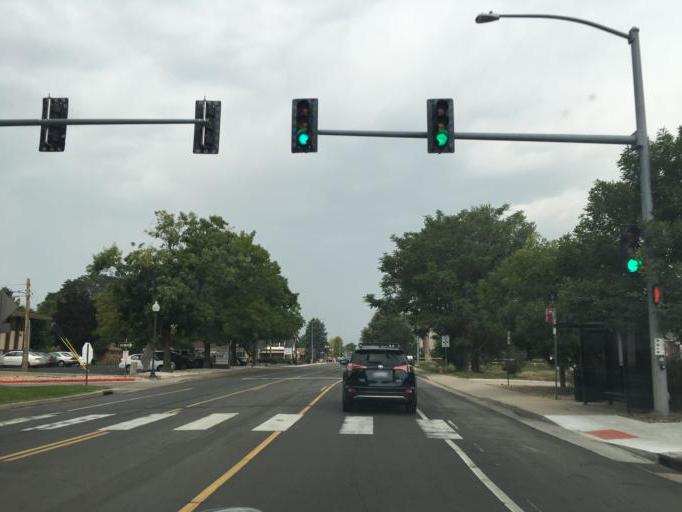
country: US
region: Colorado
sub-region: Jefferson County
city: Wheat Ridge
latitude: 39.7694
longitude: -105.0668
